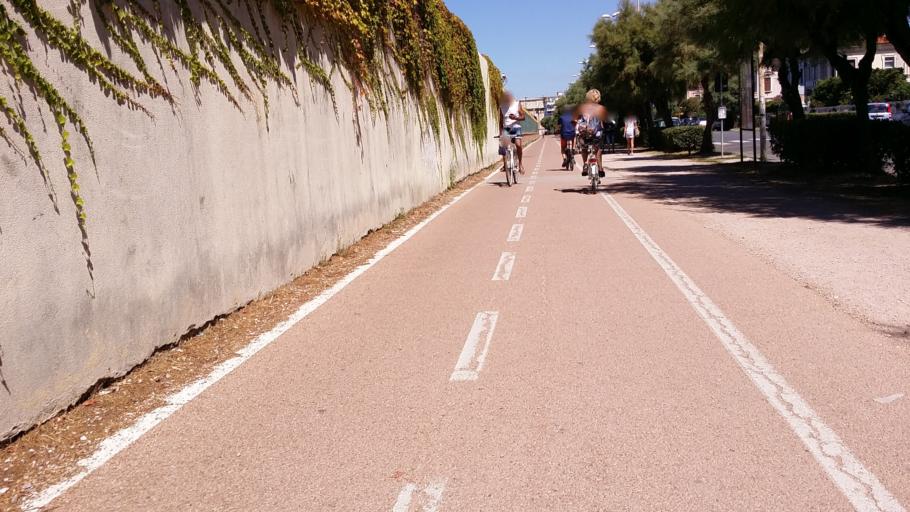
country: IT
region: Tuscany
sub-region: Provincia di Livorno
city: Livorno
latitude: 43.5249
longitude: 10.3105
